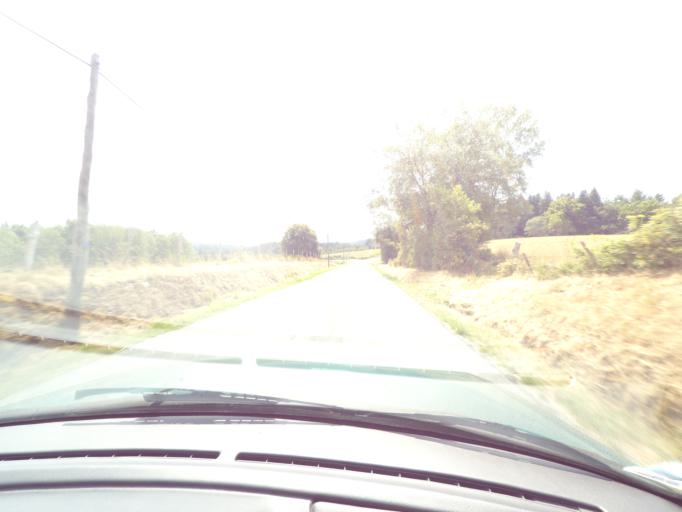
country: FR
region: Limousin
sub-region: Departement de la Correze
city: Bugeat
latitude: 45.7075
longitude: 2.0202
